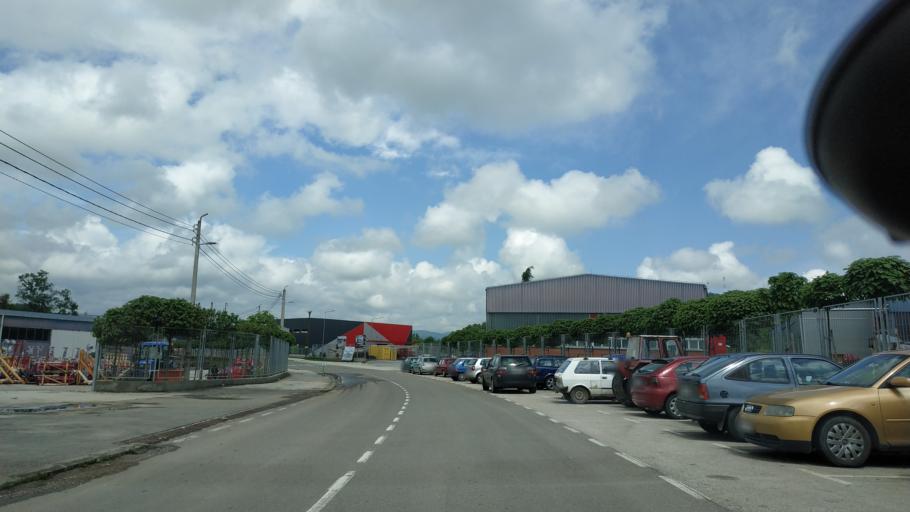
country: RS
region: Central Serbia
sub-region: Zajecarski Okrug
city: Boljevac
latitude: 43.8335
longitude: 21.9593
